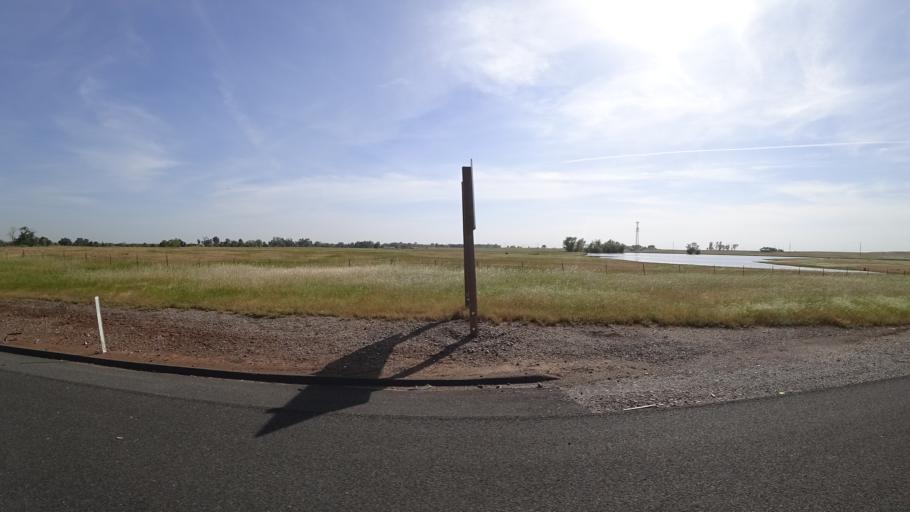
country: US
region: California
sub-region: Butte County
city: Durham
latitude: 39.6144
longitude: -121.6803
